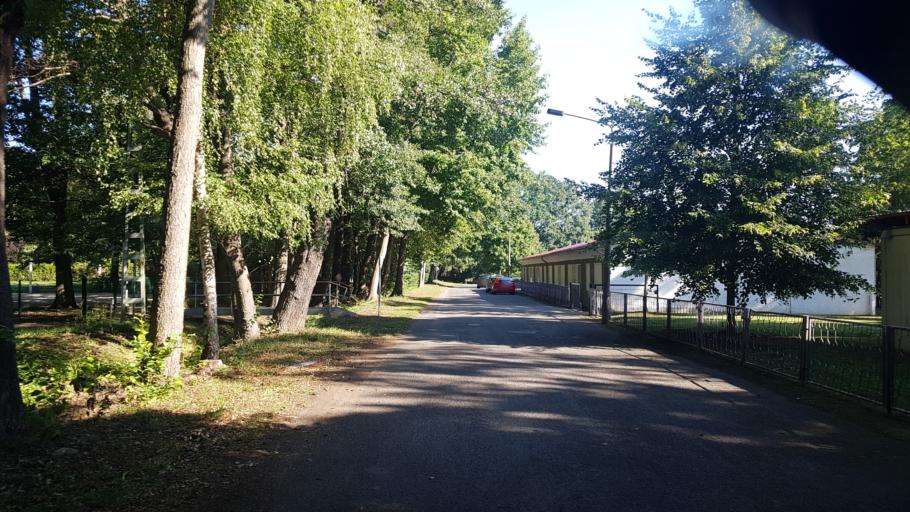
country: DE
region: Brandenburg
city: Calau
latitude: 51.7402
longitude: 13.9721
